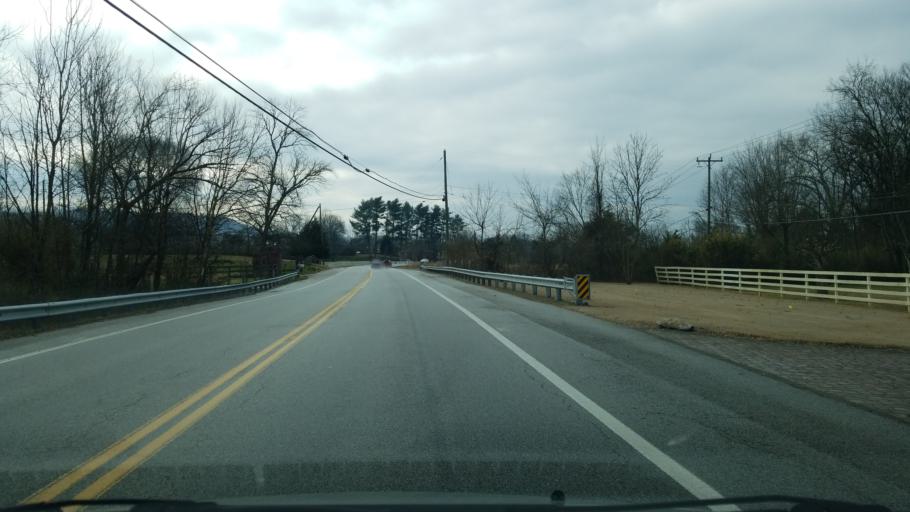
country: US
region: Tennessee
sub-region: Hamilton County
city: Collegedale
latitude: 35.0090
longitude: -85.0907
